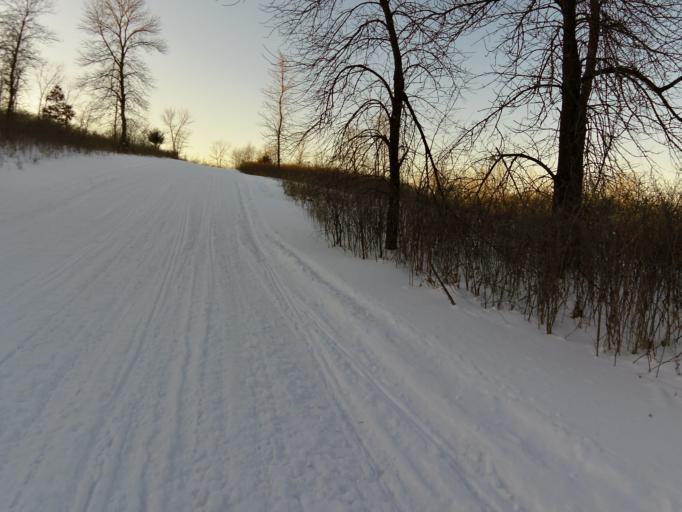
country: US
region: Minnesota
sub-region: Washington County
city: Lake Elmo
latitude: 44.9694
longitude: -92.9103
